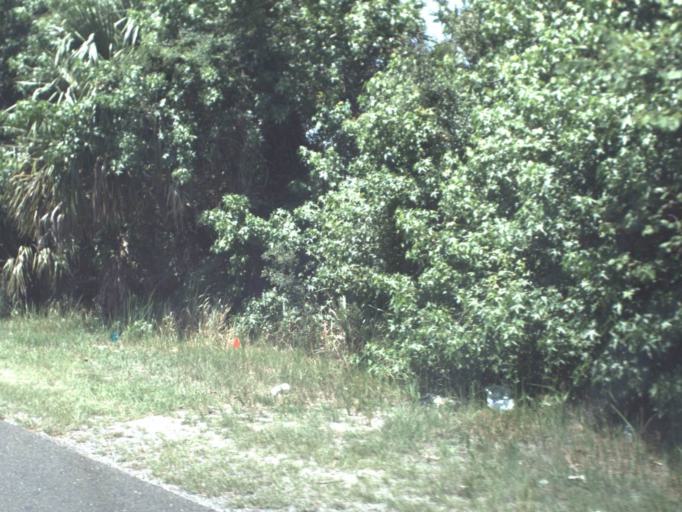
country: US
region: Florida
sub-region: Duval County
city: Jacksonville
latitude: 30.3975
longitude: -81.6487
